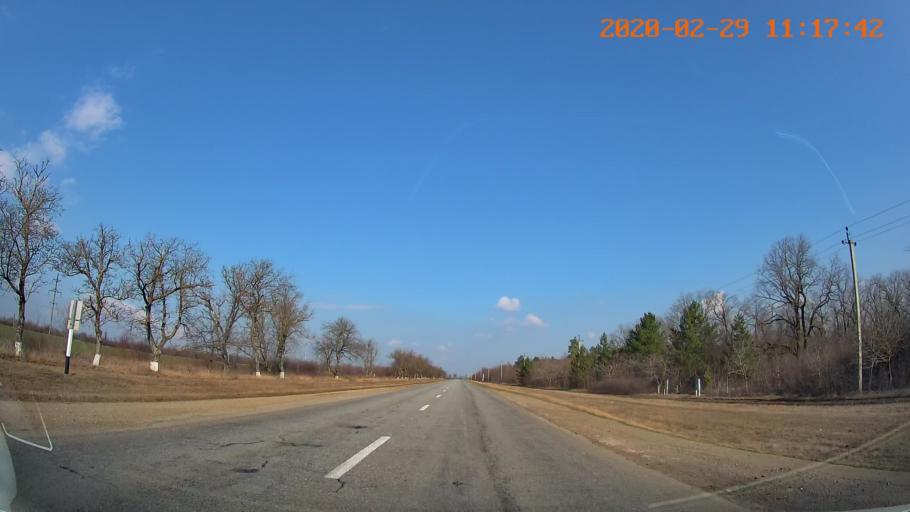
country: MD
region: Telenesti
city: Dubasari
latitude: 47.3251
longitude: 29.1713
